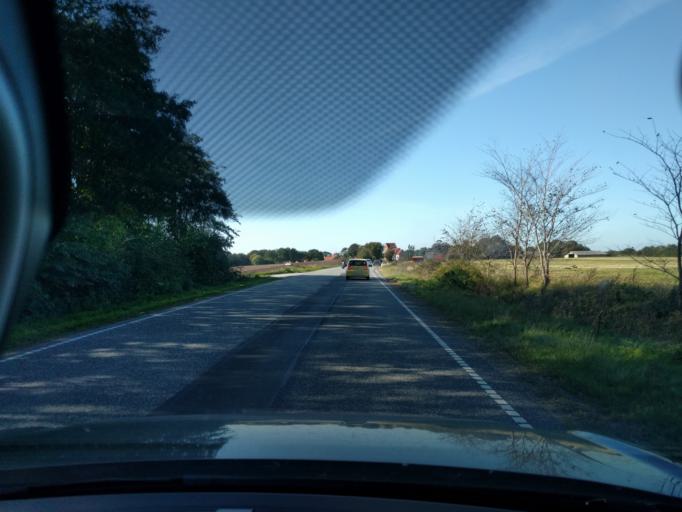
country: DK
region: North Denmark
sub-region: Mariagerfjord Kommune
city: Hobro
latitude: 56.6731
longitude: 9.6834
